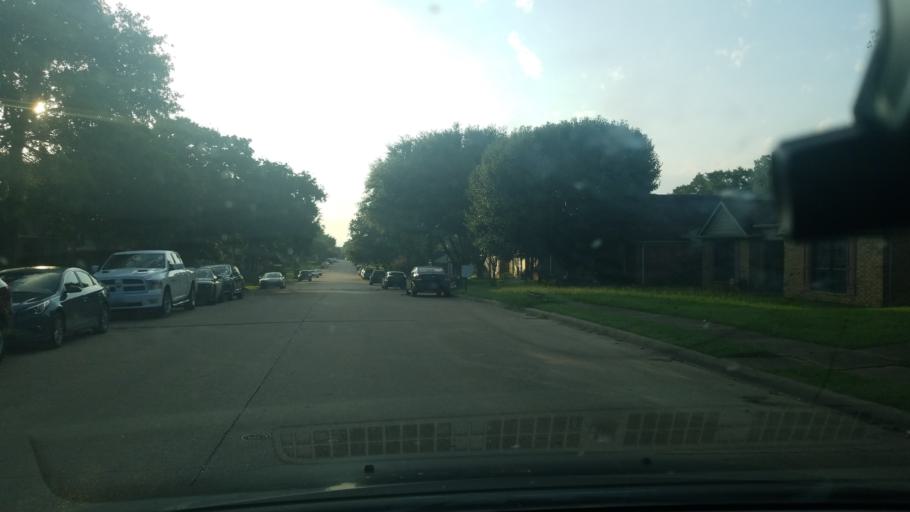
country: US
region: Texas
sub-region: Dallas County
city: Balch Springs
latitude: 32.7256
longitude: -96.6551
